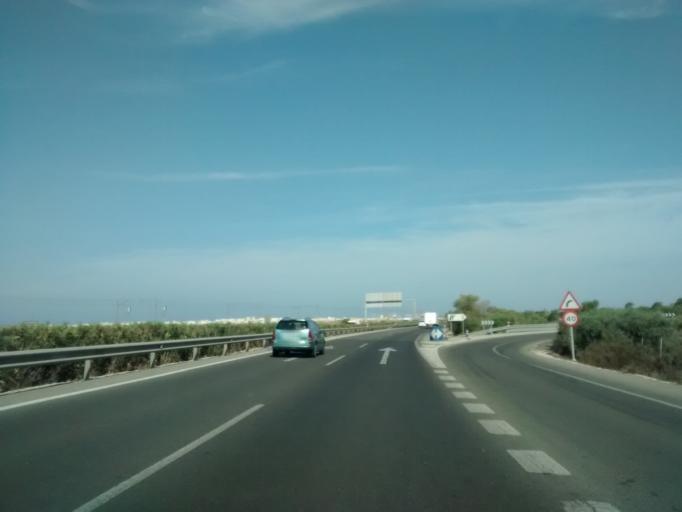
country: ES
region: Andalusia
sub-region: Provincia de Cadiz
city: Chiclana de la Frontera
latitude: 36.4444
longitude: -6.1430
